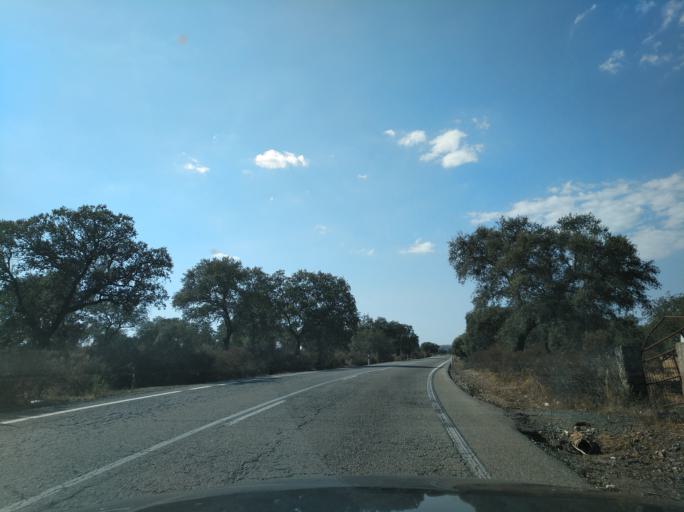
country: ES
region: Andalusia
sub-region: Provincia de Huelva
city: Santa Barbara de Casa
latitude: 37.7681
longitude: -7.1405
